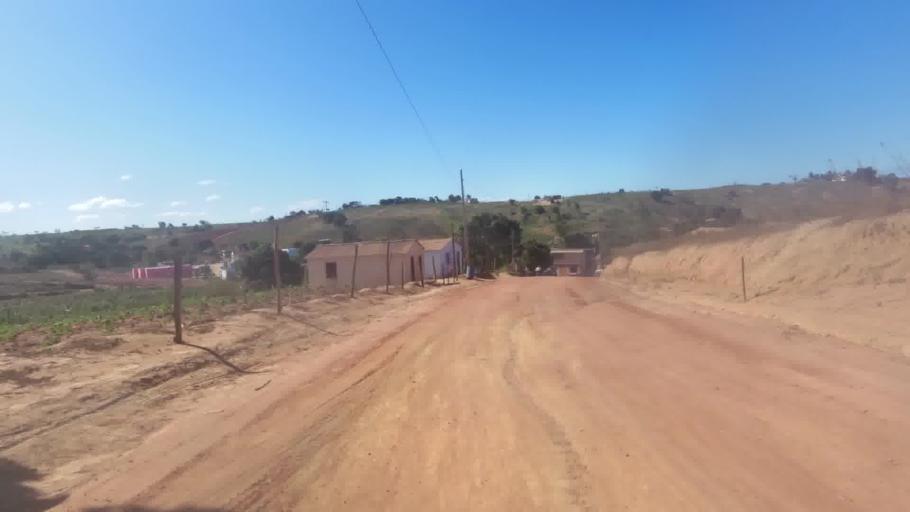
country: BR
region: Espirito Santo
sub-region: Marataizes
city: Marataizes
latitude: -21.1508
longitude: -40.9829
